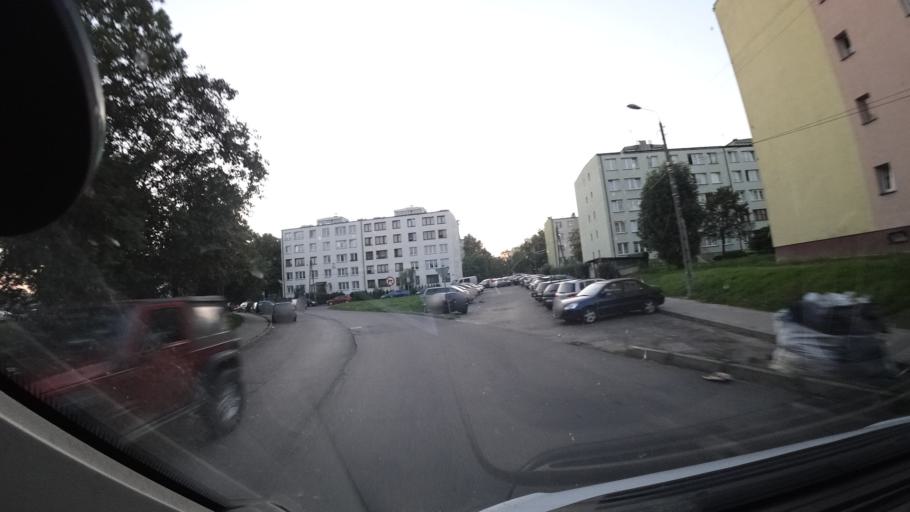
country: PL
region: Silesian Voivodeship
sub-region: Powiat tarnogorski
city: Wieszowa
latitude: 50.3656
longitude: 18.7891
